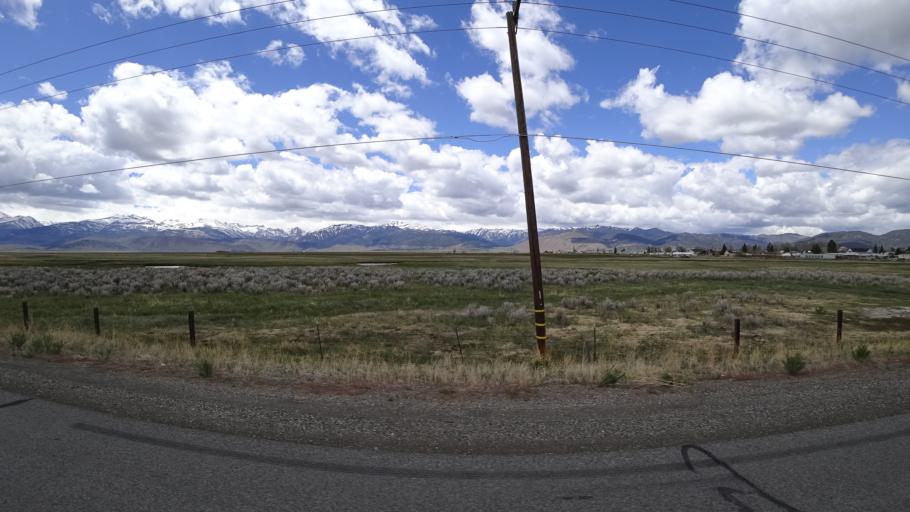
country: US
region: California
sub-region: Mono County
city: Bridgeport
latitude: 38.2528
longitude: -119.2222
